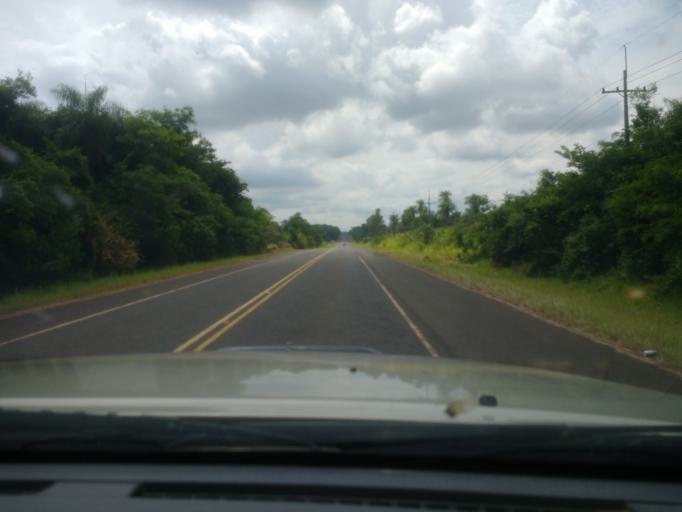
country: PY
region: San Pedro
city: Puerto Rosario
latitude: -24.4300
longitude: -57.0582
